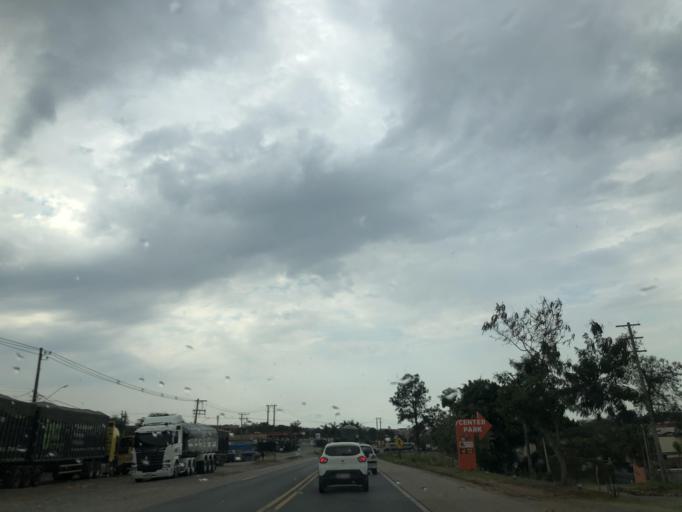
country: BR
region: Sao Paulo
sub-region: Salto De Pirapora
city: Salto de Pirapora
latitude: -23.6444
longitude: -47.5828
